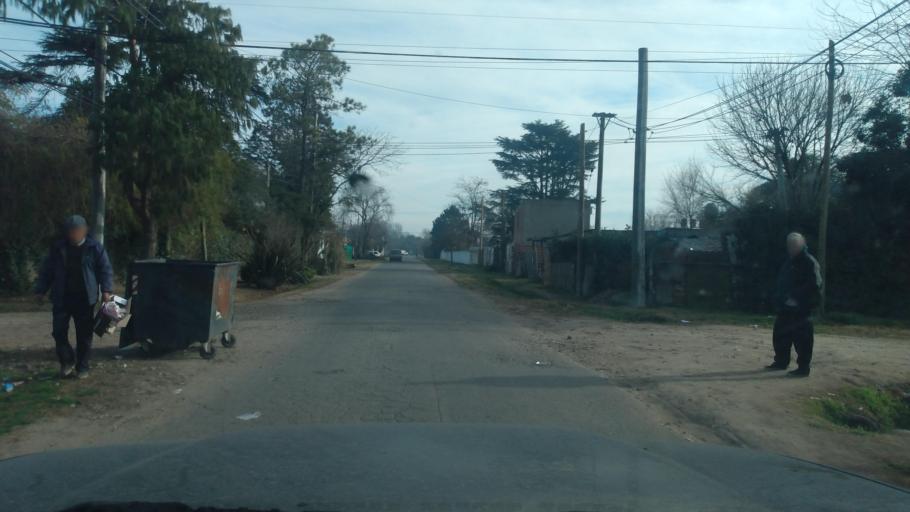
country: AR
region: Buenos Aires
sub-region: Partido de Lujan
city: Lujan
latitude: -34.5441
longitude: -59.1193
